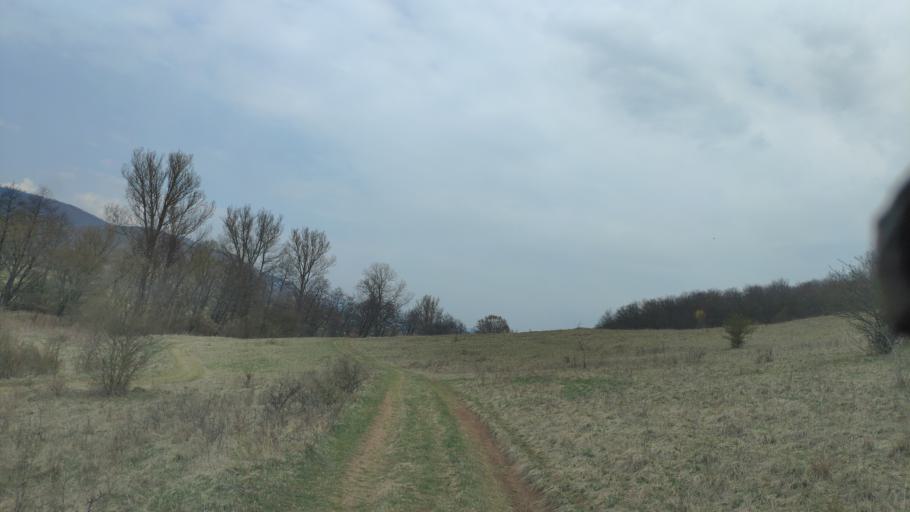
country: SK
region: Kosicky
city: Roznava
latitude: 48.6181
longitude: 20.3888
